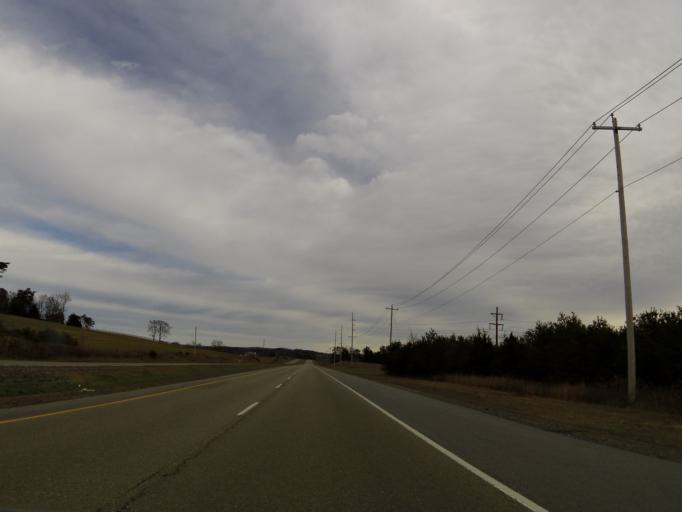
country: US
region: Tennessee
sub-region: Cocke County
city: Newport
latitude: 35.9952
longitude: -83.1091
